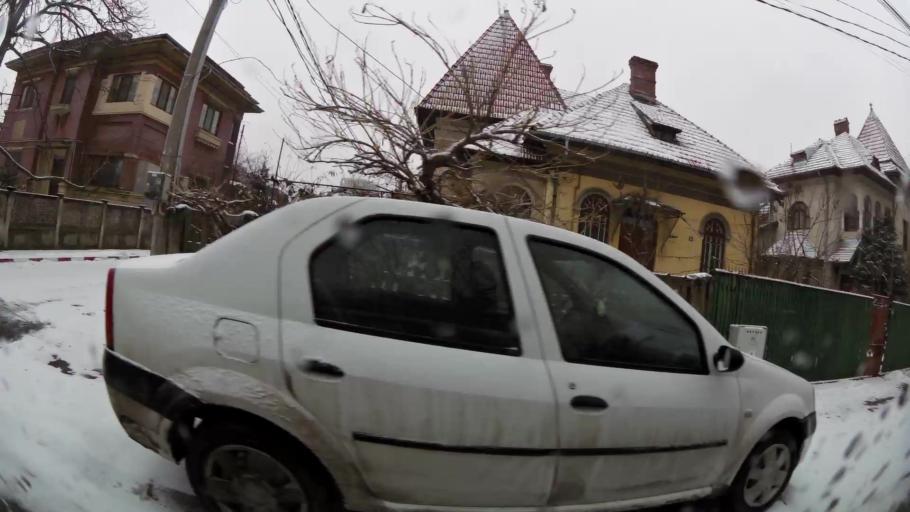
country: RO
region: Dambovita
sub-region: Municipiul Targoviste
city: Targoviste
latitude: 44.9298
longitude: 25.4637
